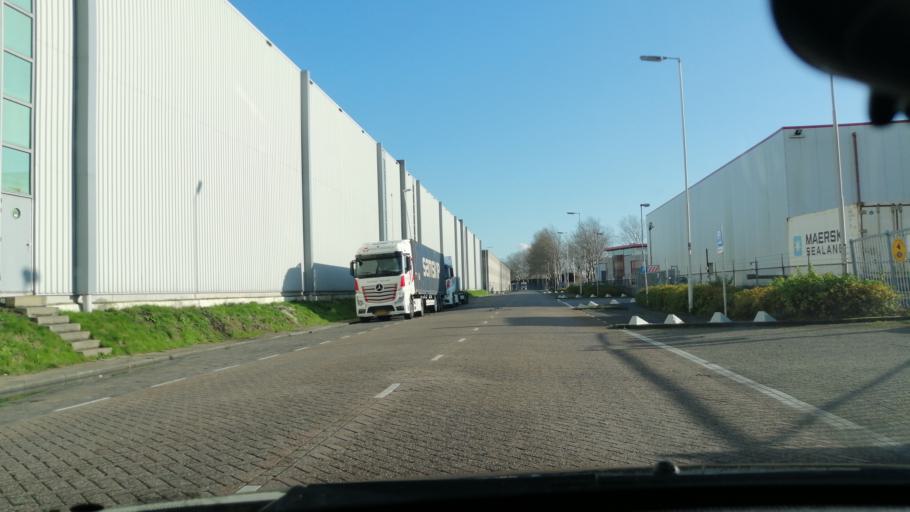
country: NL
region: South Holland
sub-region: Gemeente Albrandswaard
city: Rhoon
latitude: 51.8687
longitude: 4.4167
